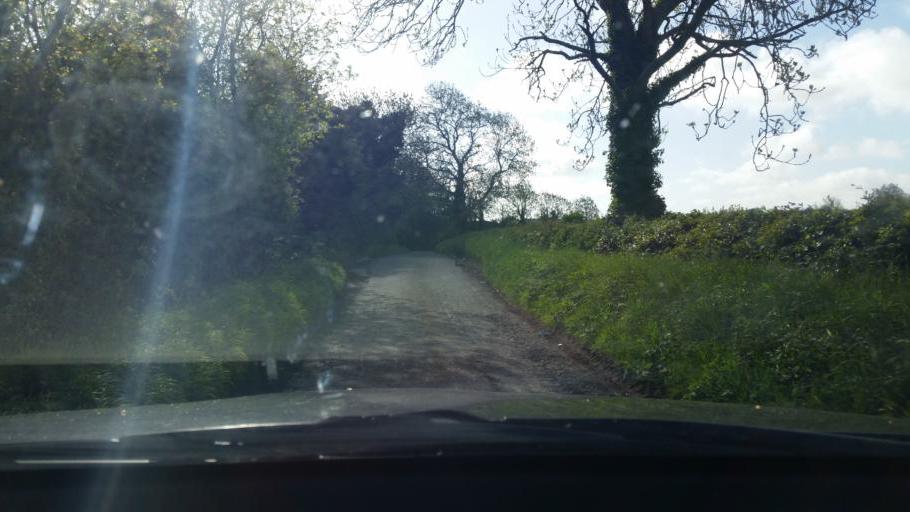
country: IE
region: Leinster
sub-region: Fingal County
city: Blanchardstown
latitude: 53.4250
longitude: -6.3503
